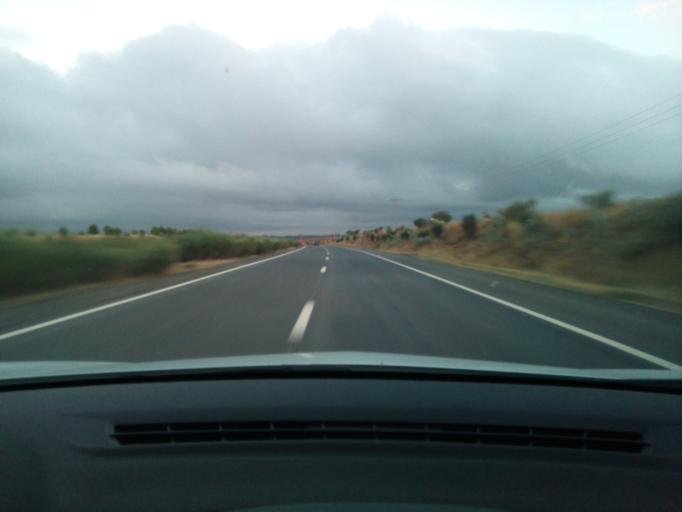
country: MA
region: Meknes-Tafilalet
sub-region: Meknes
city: Meknes
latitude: 33.8522
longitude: -5.6247
